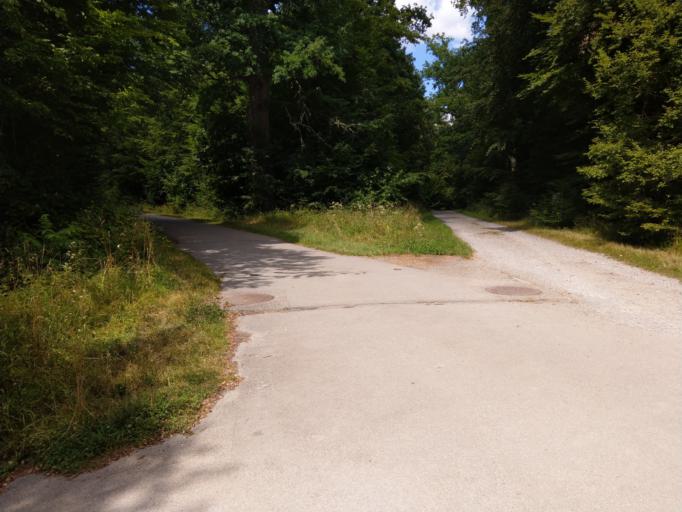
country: DE
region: Baden-Wuerttemberg
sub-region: Regierungsbezirk Stuttgart
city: Gerlingen
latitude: 48.7582
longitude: 9.1023
